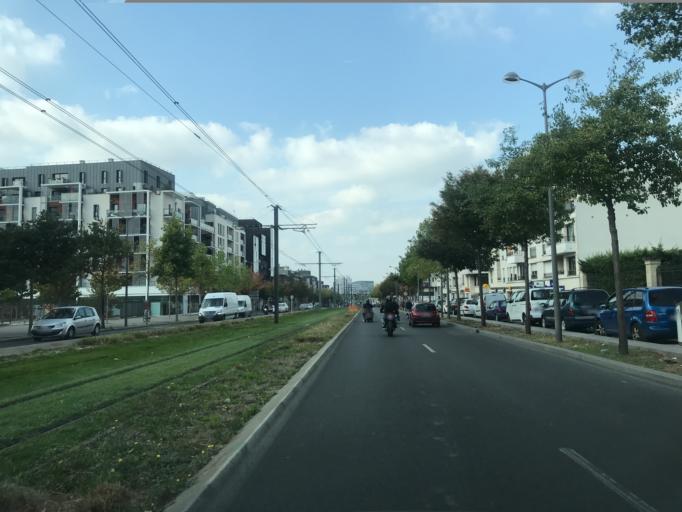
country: FR
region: Ile-de-France
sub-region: Departement du Val-d'Oise
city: Bezons
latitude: 48.9152
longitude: 2.2282
